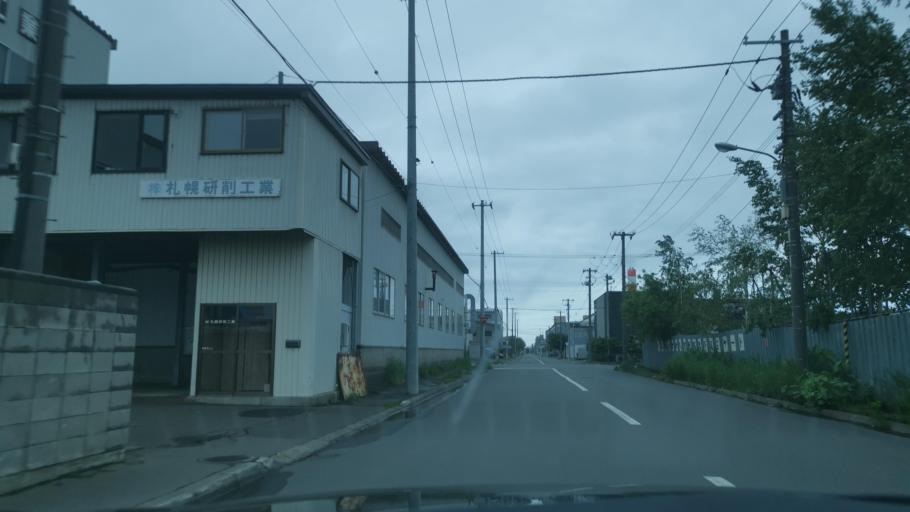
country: JP
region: Hokkaido
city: Sapporo
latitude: 43.1037
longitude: 141.2898
